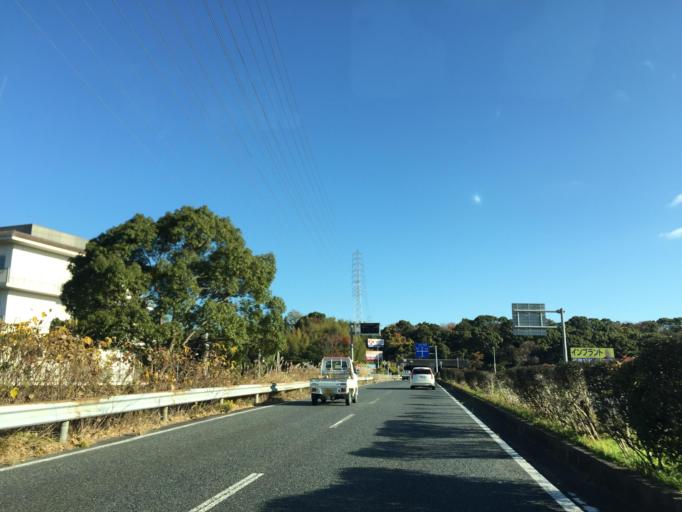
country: JP
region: Wakayama
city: Iwade
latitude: 34.3581
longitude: 135.2664
